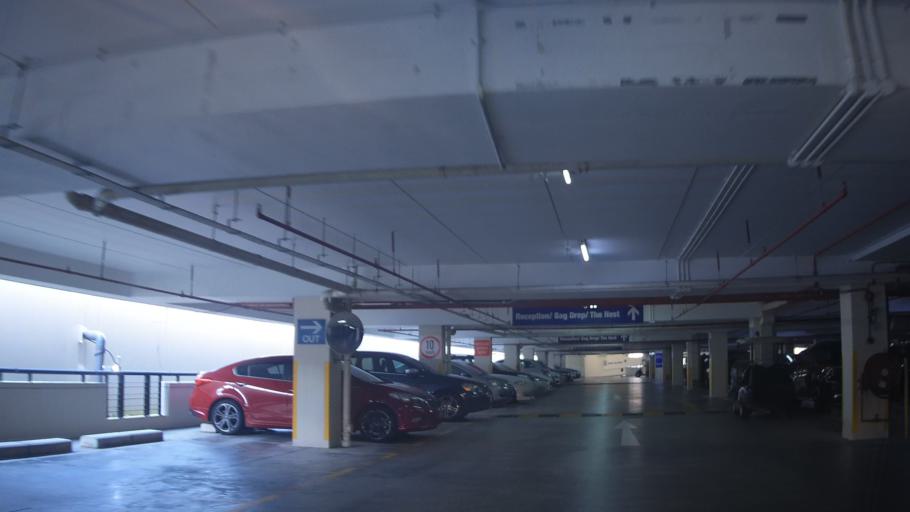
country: SG
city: Singapore
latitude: 1.3215
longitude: 103.9633
